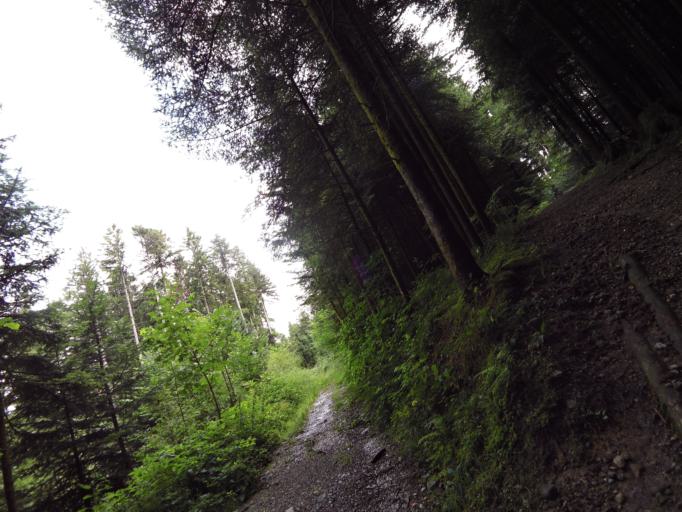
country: DE
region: Bavaria
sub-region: Swabia
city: Heimenkirch
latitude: 47.6078
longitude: 9.9080
